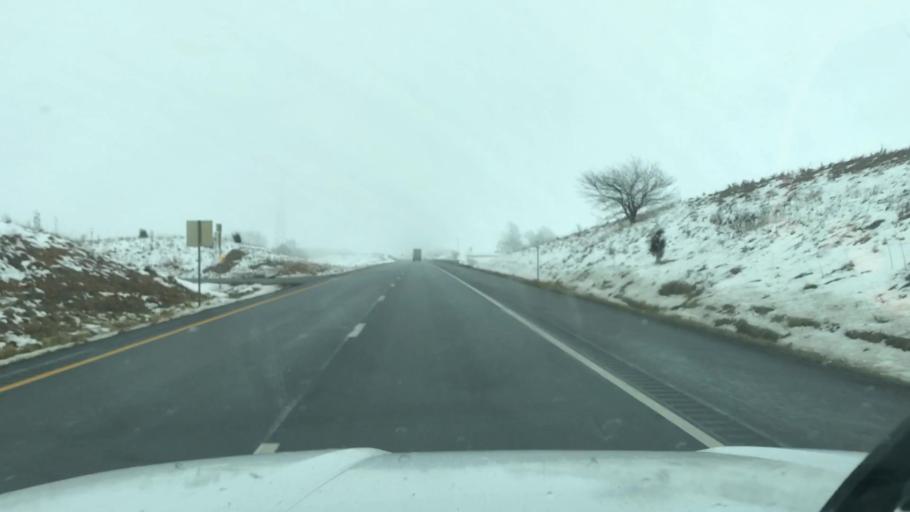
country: US
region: Missouri
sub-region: Clinton County
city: Gower
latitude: 39.7616
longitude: -94.5429
